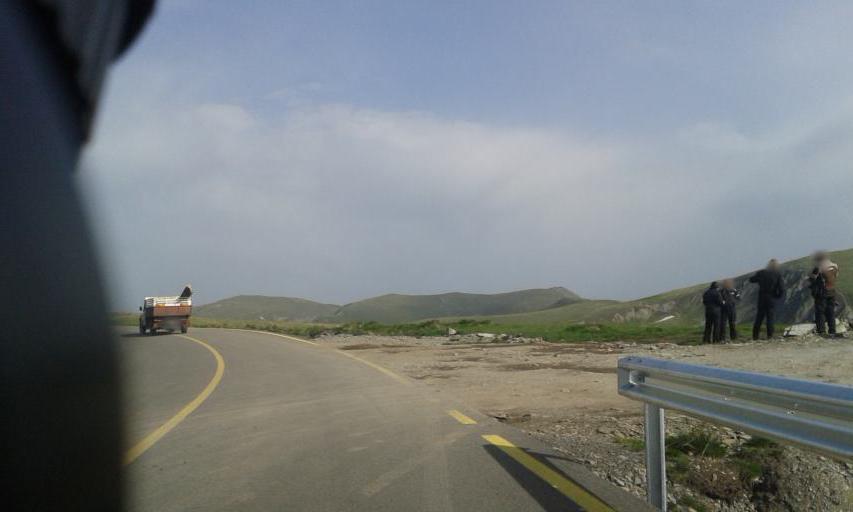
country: RO
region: Gorj
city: Novaci-Straini
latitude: 45.3635
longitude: 23.6527
